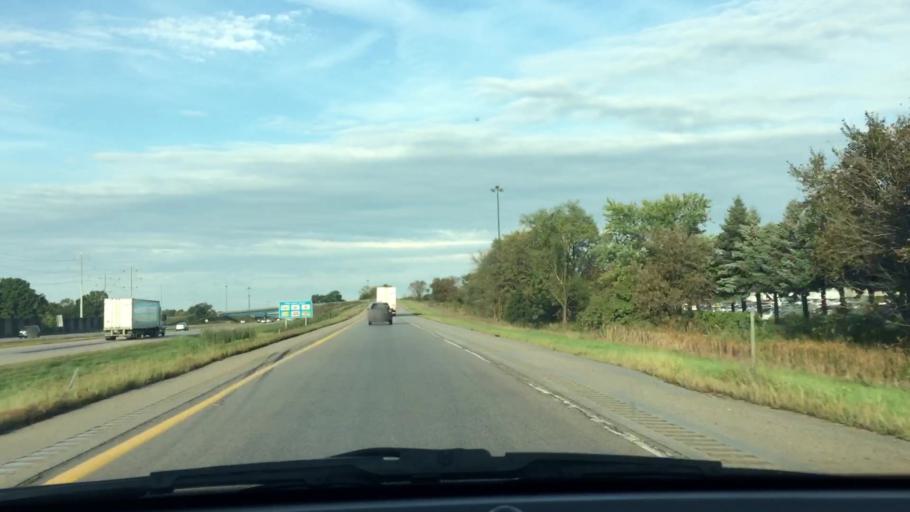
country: US
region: Illinois
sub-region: Winnebago County
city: Cherry Valley
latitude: 42.2198
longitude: -88.9998
